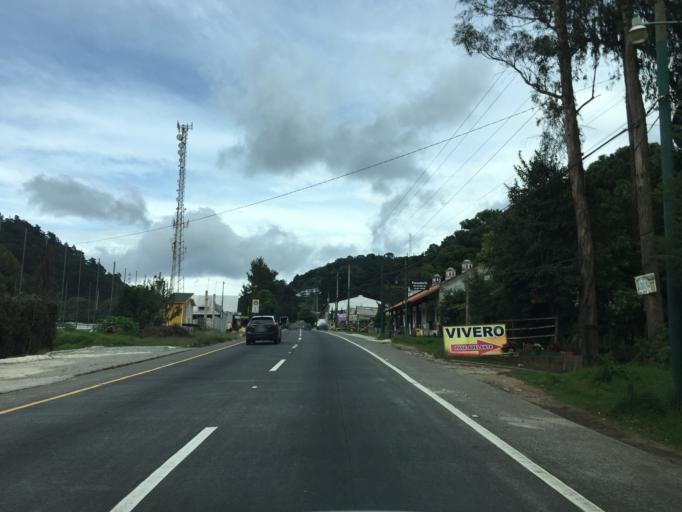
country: GT
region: Sacatepequez
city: Santa Lucia Milpas Altas
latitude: 14.5747
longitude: -90.6688
